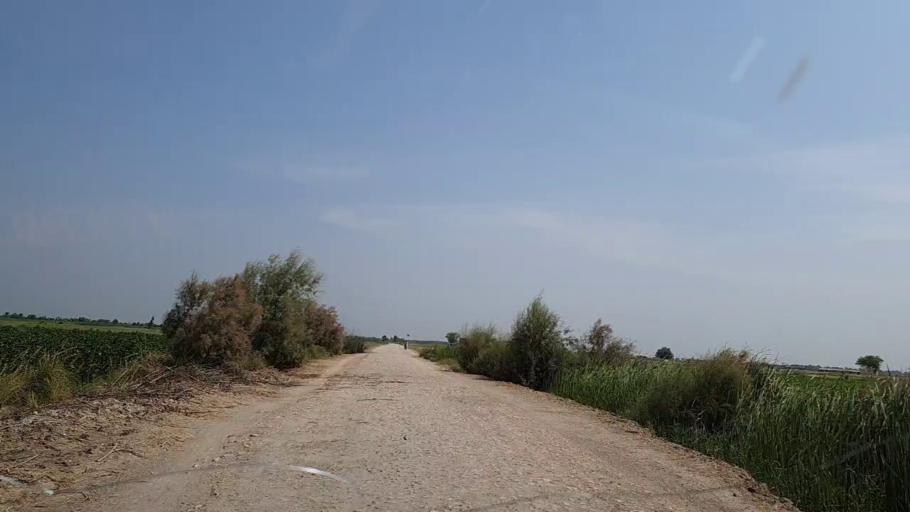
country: PK
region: Sindh
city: Khanpur
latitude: 27.8011
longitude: 69.3128
